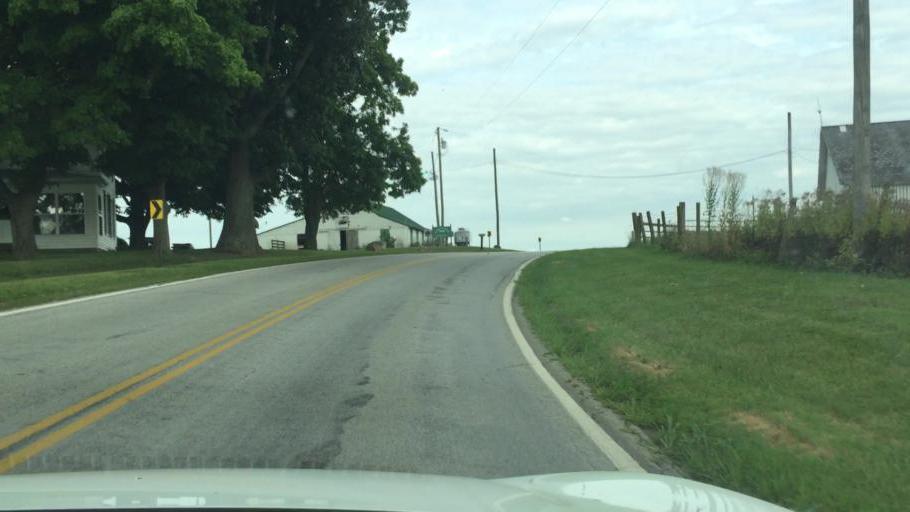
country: US
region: Ohio
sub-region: Clark County
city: Northridge
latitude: 39.9906
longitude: -83.6884
